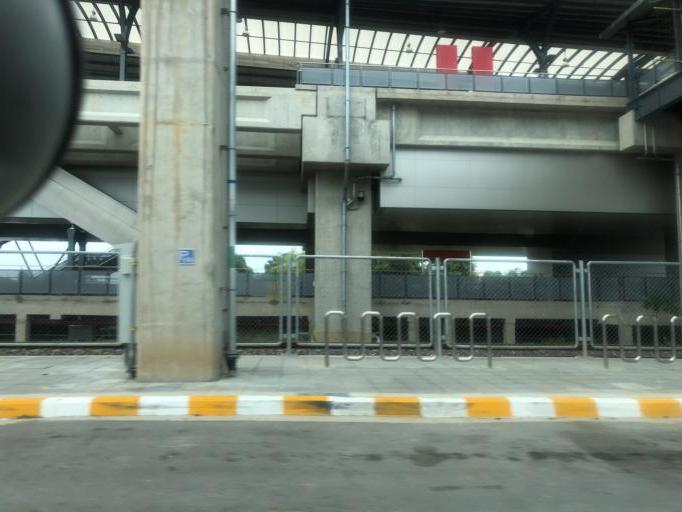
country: TH
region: Bangkok
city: Don Mueang
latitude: 13.9652
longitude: 100.6051
